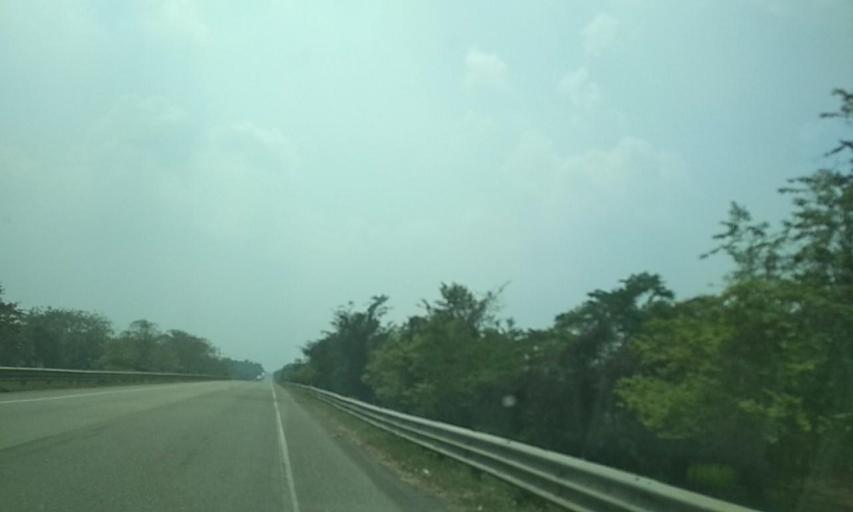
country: MX
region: Tabasco
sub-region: Huimanguillo
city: Francisco Rueda
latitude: 17.7631
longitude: -94.0156
